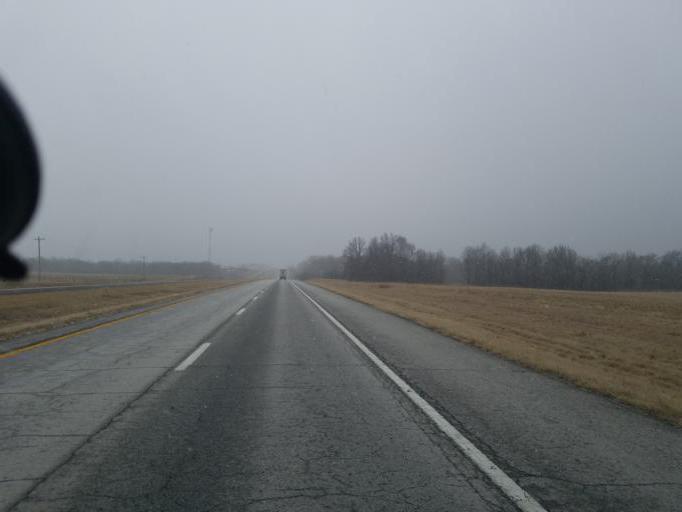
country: US
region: Missouri
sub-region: Macon County
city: La Plata
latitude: 39.9279
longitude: -92.4760
